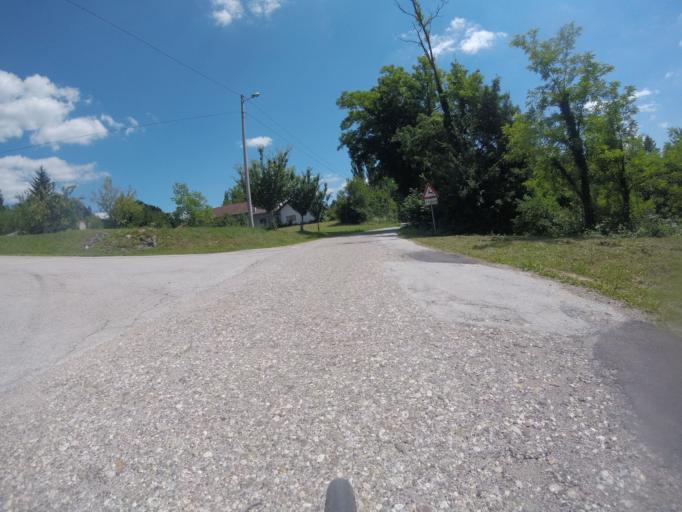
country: HR
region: Karlovacka
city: Ozalj
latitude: 45.6695
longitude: 15.4749
